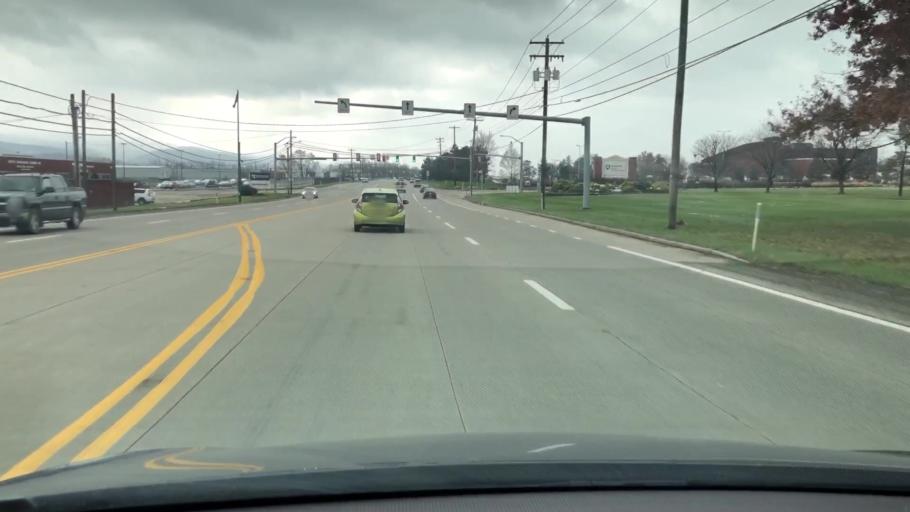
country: US
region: Pennsylvania
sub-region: Fayette County
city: Dunbar
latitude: 39.9474
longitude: -79.6553
